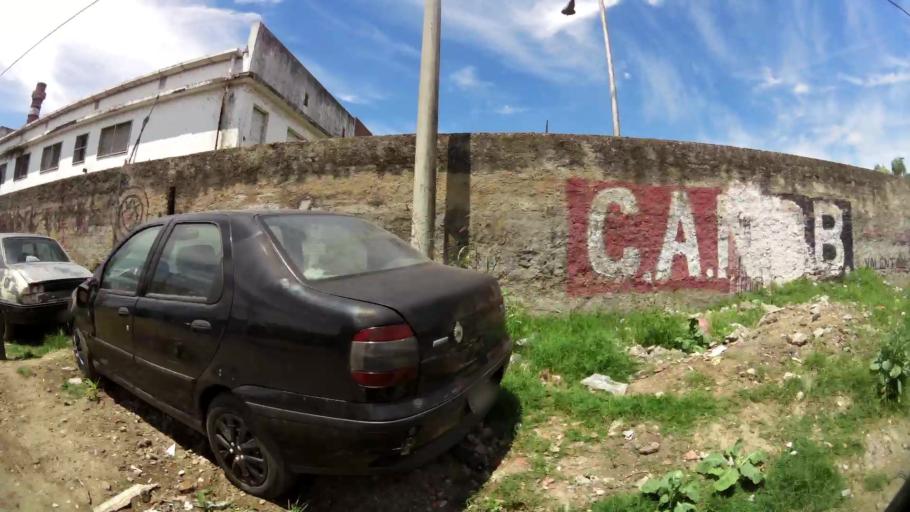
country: AR
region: Santa Fe
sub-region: Departamento de Rosario
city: Rosario
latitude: -32.9766
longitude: -60.6264
